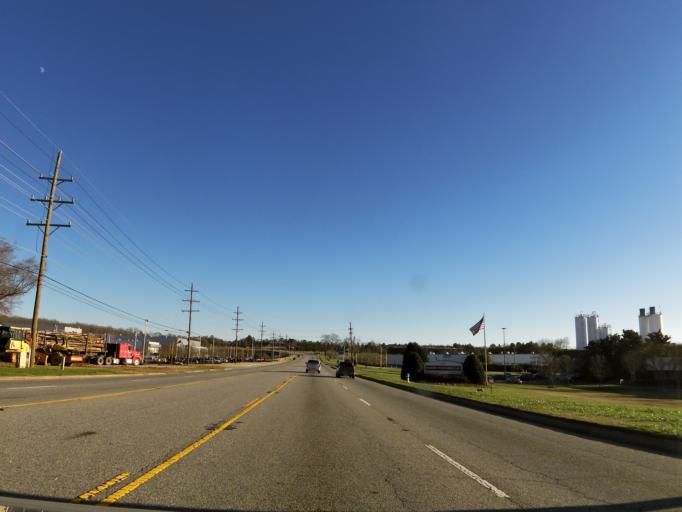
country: US
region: South Carolina
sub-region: Spartanburg County
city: Wellford
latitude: 34.9004
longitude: -82.0949
